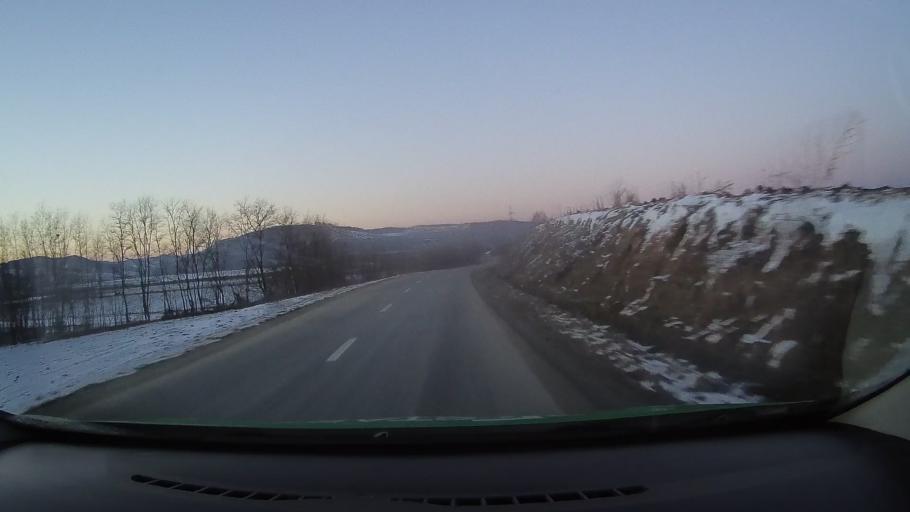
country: RO
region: Sibiu
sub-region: Comuna Alma
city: Alma
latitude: 46.1908
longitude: 24.4706
